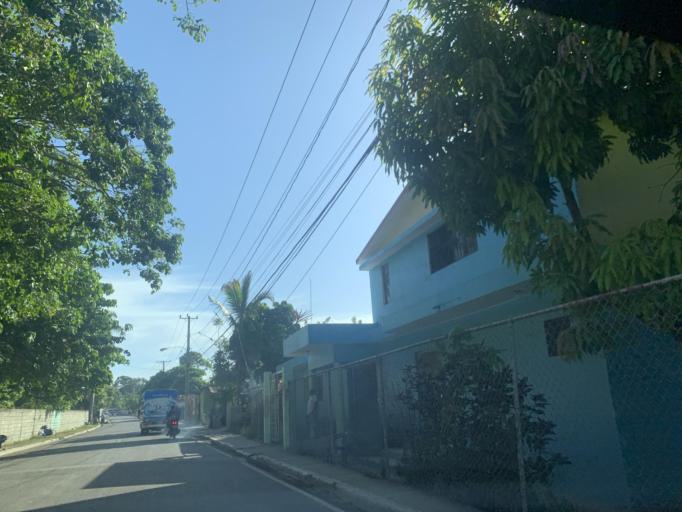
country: DO
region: Puerto Plata
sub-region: Puerto Plata
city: Puerto Plata
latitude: 19.8041
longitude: -70.7160
